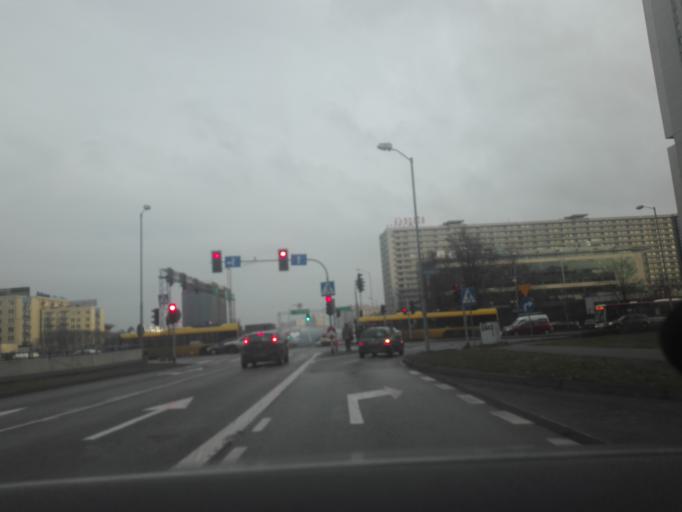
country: PL
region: Silesian Voivodeship
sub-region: Katowice
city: Katowice
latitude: 50.2653
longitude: 19.0181
